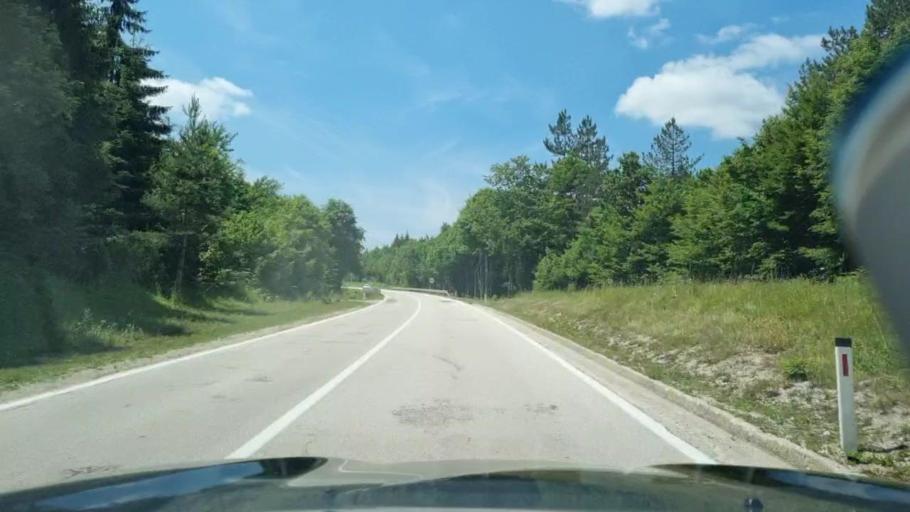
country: BA
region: Federation of Bosnia and Herzegovina
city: Sanica
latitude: 44.5498
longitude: 16.6400
